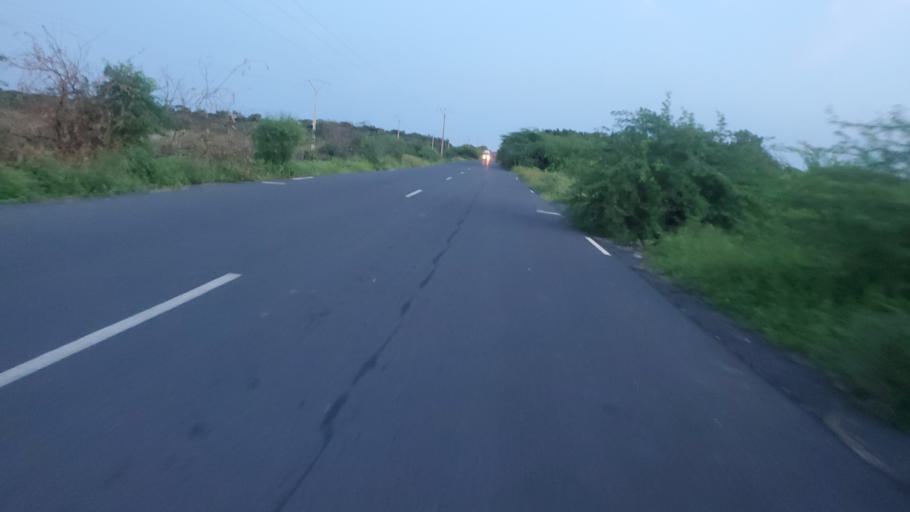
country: SN
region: Saint-Louis
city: Saint-Louis
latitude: 16.0811
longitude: -16.3920
